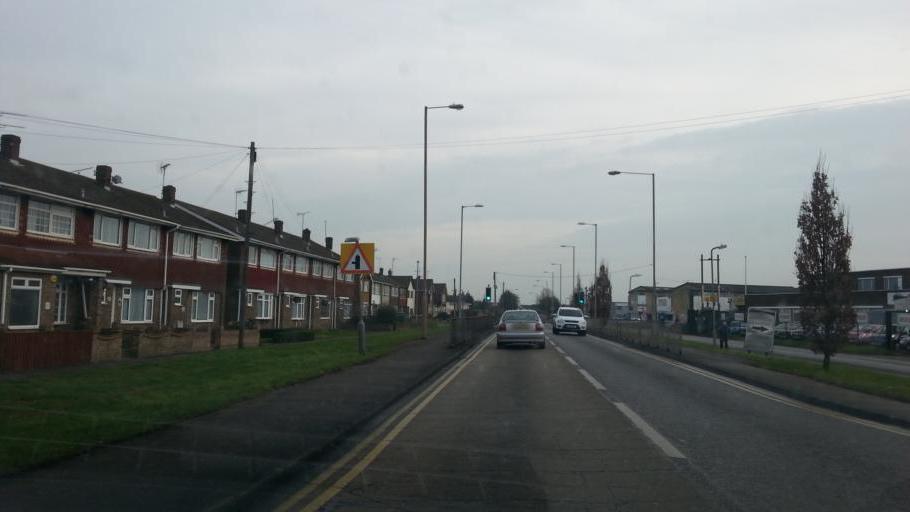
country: GB
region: England
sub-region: Essex
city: Canvey Island
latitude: 51.5225
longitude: 0.5584
